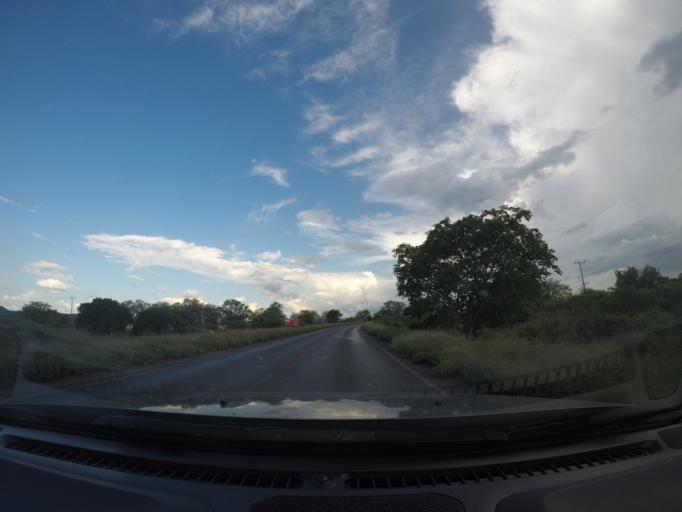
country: BR
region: Bahia
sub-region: Ibotirama
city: Ibotirama
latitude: -12.1427
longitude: -43.3179
